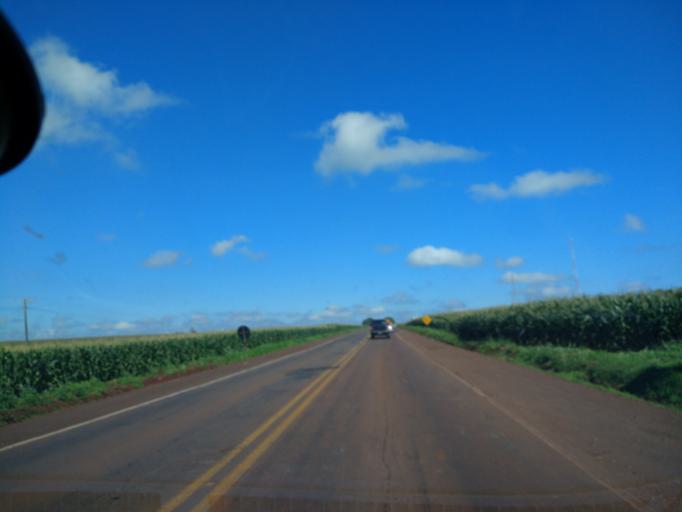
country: BR
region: Parana
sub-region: Terra Boa
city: Terra Boa
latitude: -23.6387
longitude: -52.4742
